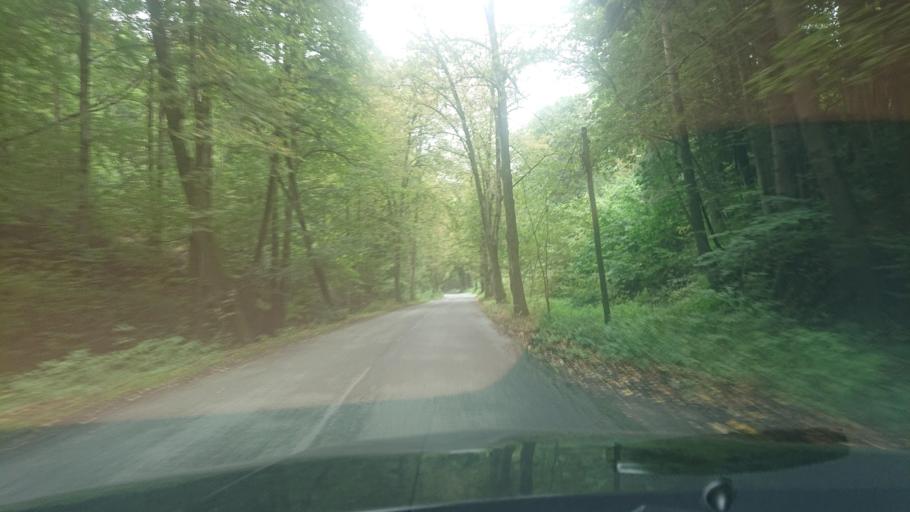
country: PL
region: Lower Silesian Voivodeship
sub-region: Powiat klodzki
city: Bystrzyca Klodzka
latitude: 50.3167
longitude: 16.7108
